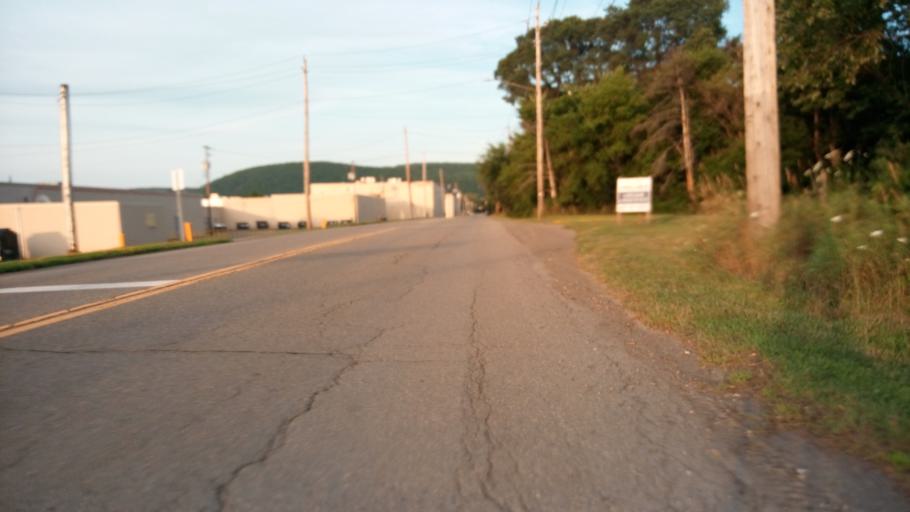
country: US
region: New York
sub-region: Chemung County
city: Horseheads
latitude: 42.1565
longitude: -76.8287
